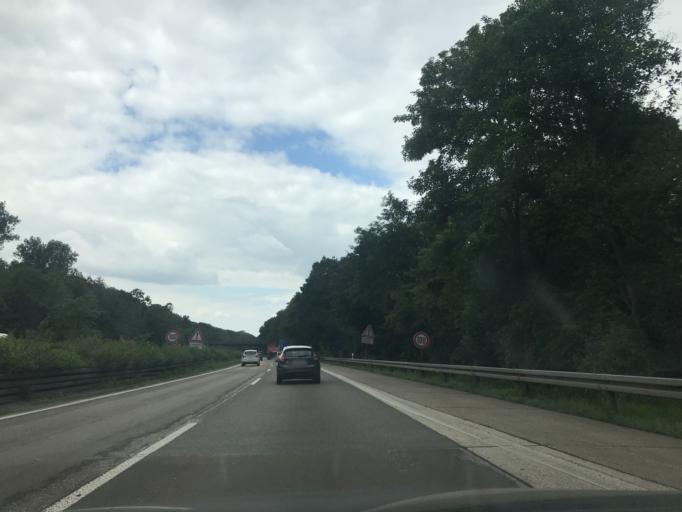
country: DE
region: North Rhine-Westphalia
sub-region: Regierungsbezirk Dusseldorf
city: Erkrath
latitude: 51.1799
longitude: 6.8820
